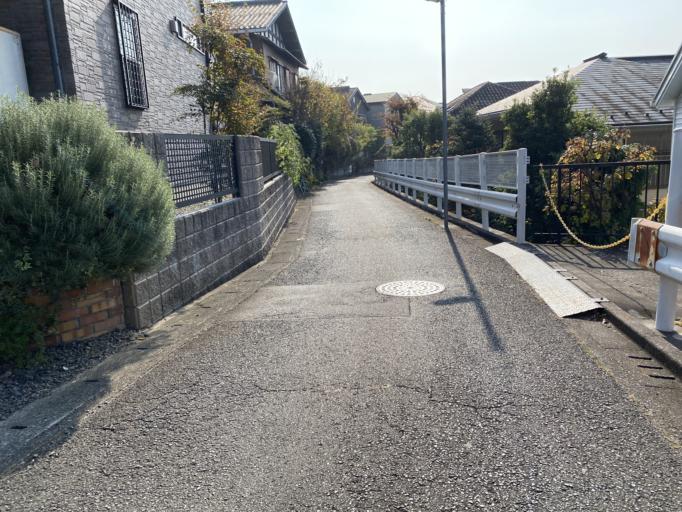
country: JP
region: Tokyo
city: Chofugaoka
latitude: 35.6098
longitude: 139.5028
